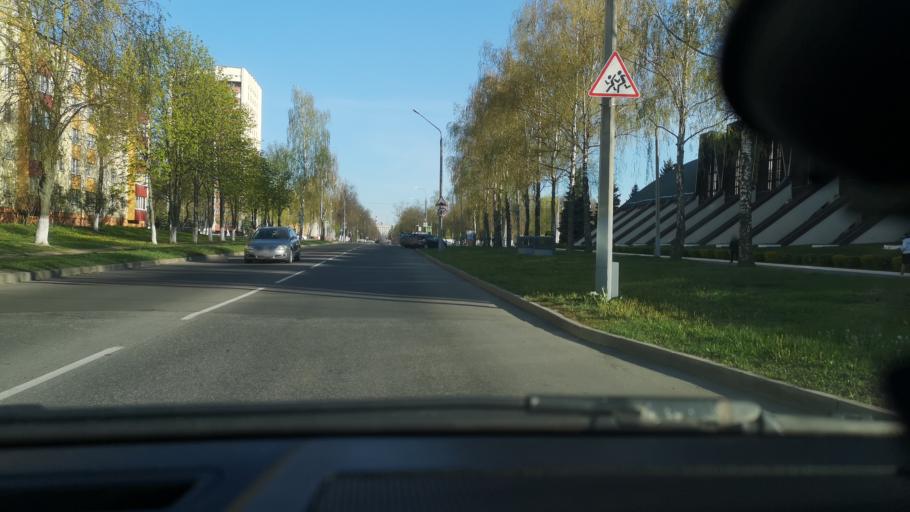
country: BY
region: Gomel
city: Gomel
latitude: 52.4516
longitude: 31.0068
